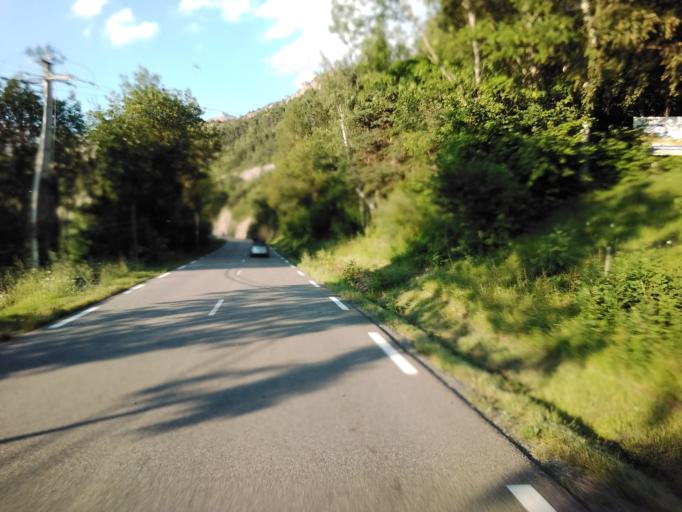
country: FR
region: Provence-Alpes-Cote d'Azur
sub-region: Departement des Alpes-de-Haute-Provence
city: Seyne-les-Alpes
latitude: 44.4439
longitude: 6.3664
